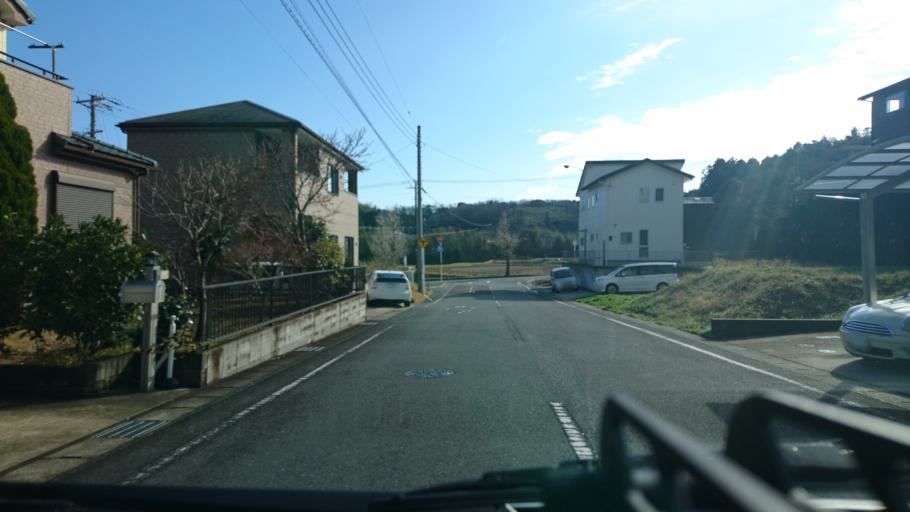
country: JP
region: Chiba
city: Kisarazu
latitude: 35.3487
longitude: 139.9477
